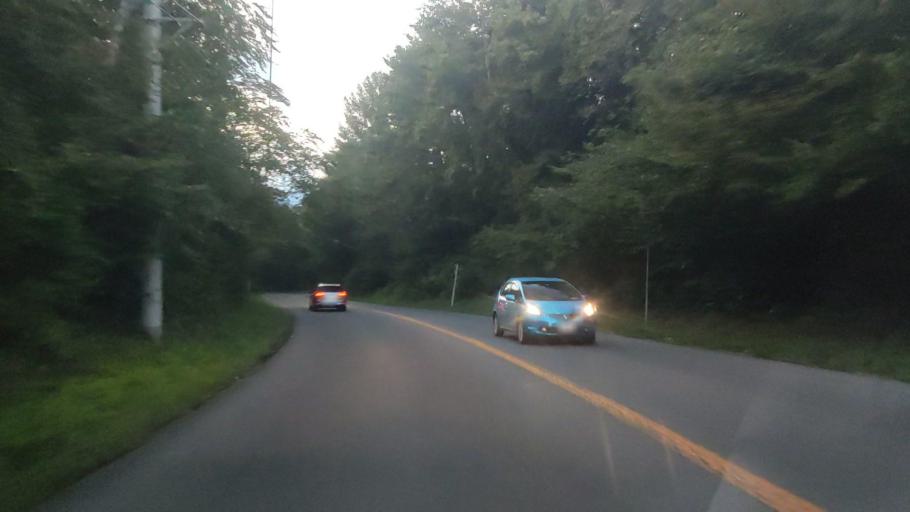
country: JP
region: Gunma
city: Nakanojomachi
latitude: 36.5324
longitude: 138.6104
